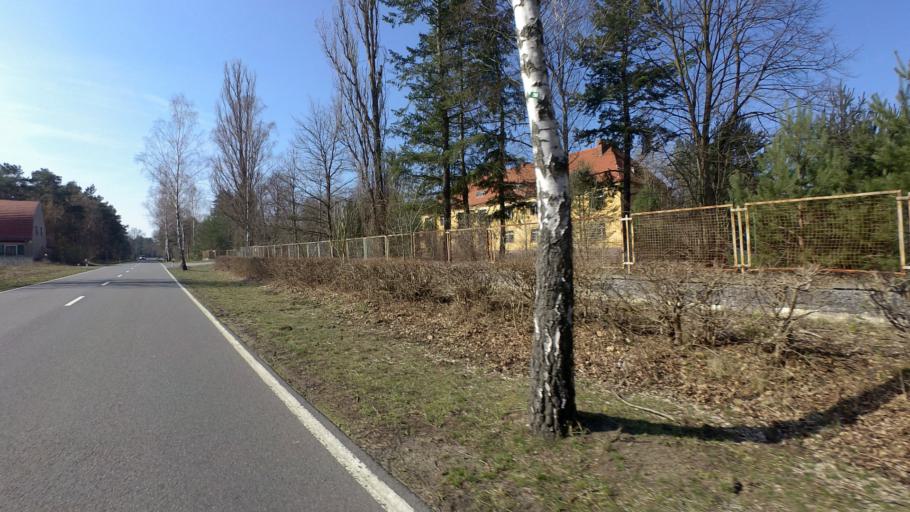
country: DE
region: Brandenburg
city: Sperenberg
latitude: 52.0956
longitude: 13.3640
